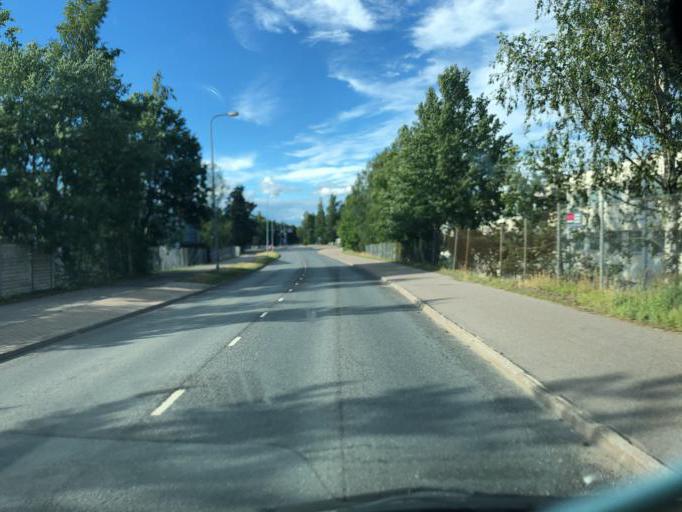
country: FI
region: Uusimaa
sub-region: Helsinki
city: Vantaa
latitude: 60.2843
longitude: 25.0800
